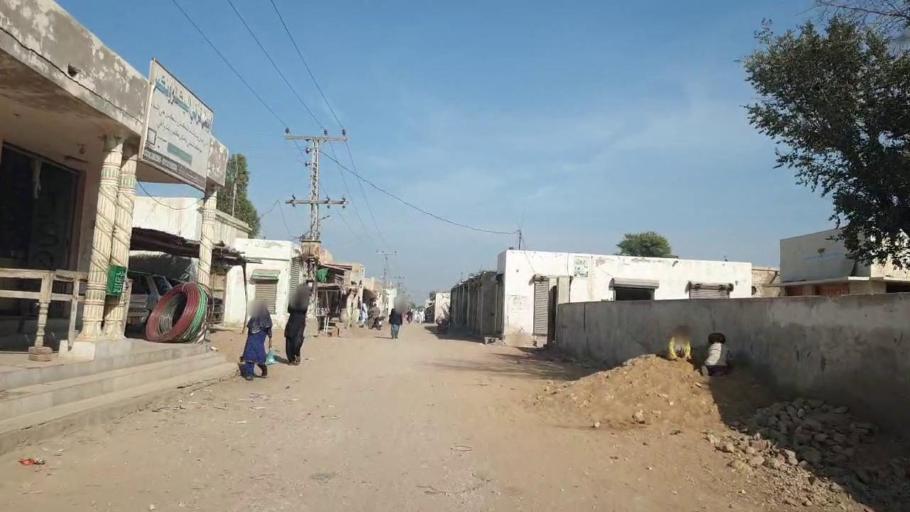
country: PK
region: Sindh
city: Sann
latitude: 25.9076
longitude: 68.2362
